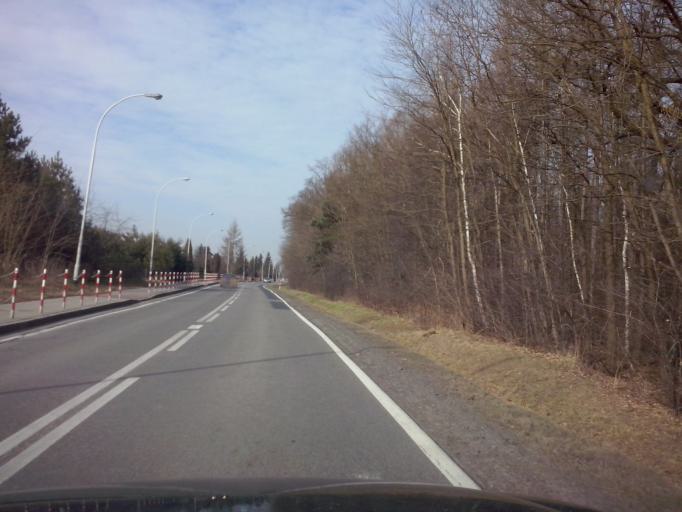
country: PL
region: Subcarpathian Voivodeship
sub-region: Powiat nizanski
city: Rudnik nad Sanem
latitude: 50.4247
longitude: 22.2765
